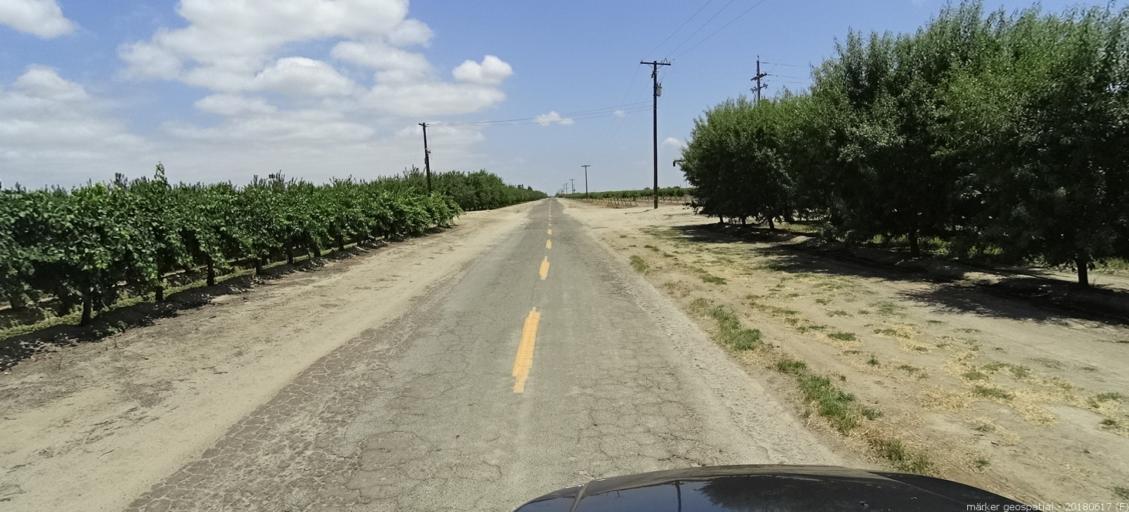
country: US
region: California
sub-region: Fresno County
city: Kerman
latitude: 36.8222
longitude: -120.1605
